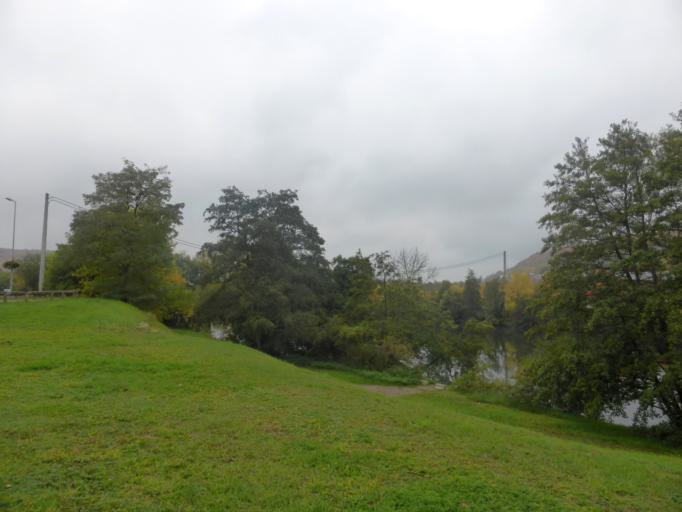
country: FR
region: Lorraine
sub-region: Departement de Meurthe-et-Moselle
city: Frouard
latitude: 48.7703
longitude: 6.1350
